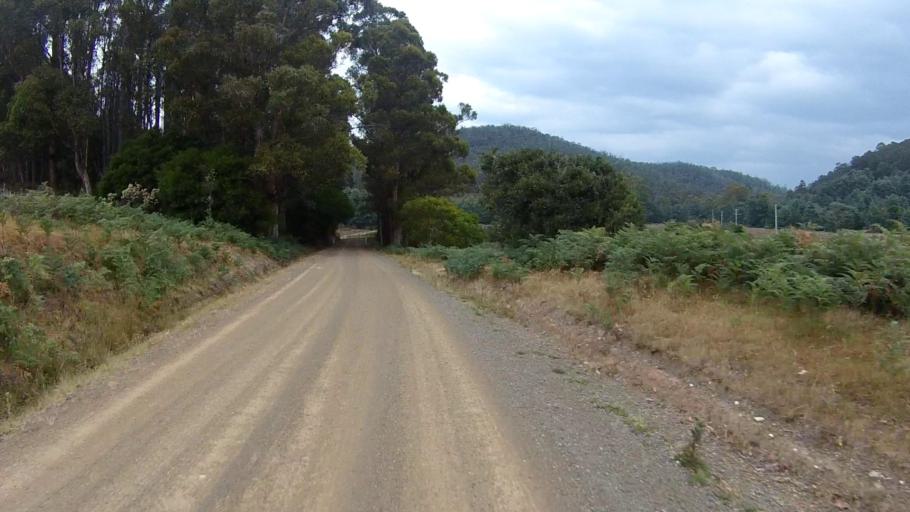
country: AU
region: Tasmania
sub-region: Kingborough
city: Kettering
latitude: -43.2182
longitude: 147.1763
